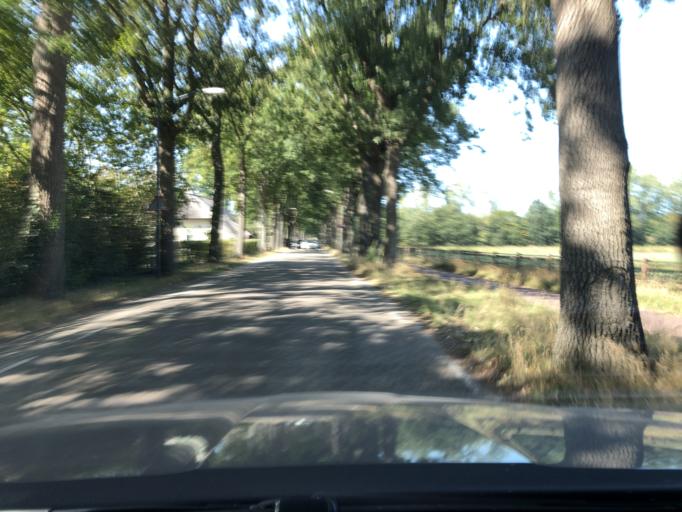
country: NL
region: North Brabant
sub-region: Gemeente Vught
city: Vught
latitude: 51.6572
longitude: 5.2417
